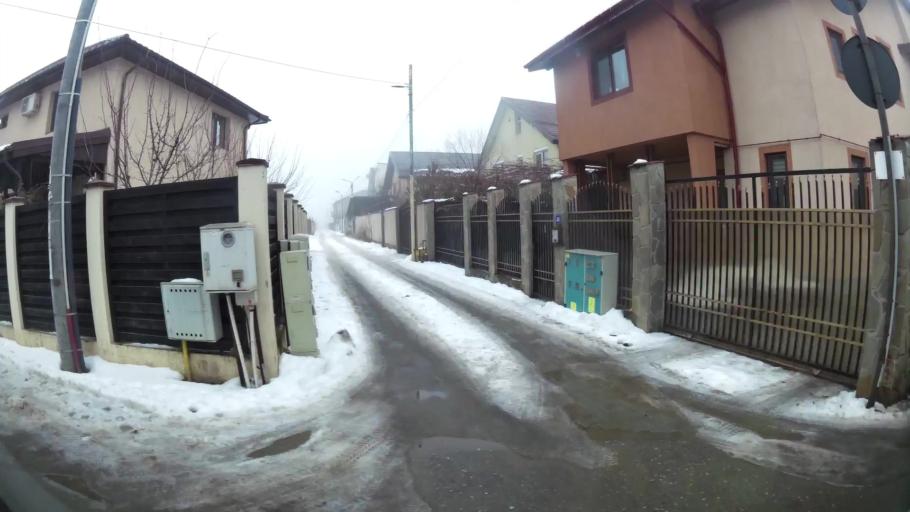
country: RO
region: Ilfov
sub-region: Comuna Chiajna
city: Chiajna
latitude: 44.4518
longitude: 25.9775
